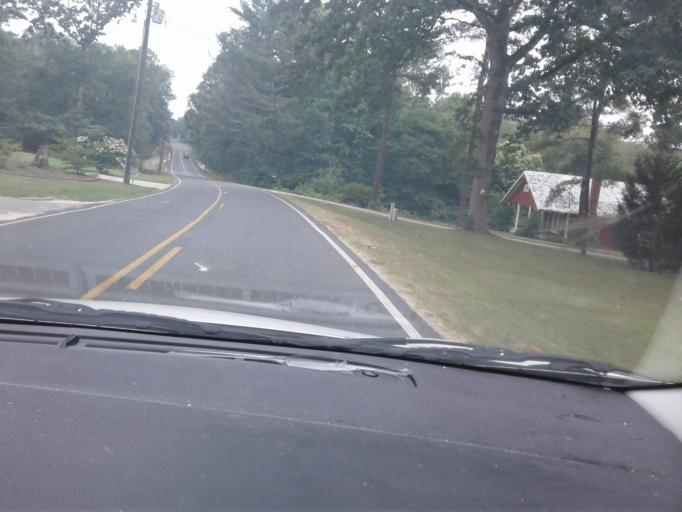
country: US
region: North Carolina
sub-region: Harnett County
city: Buies Creek
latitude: 35.4114
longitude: -78.7261
